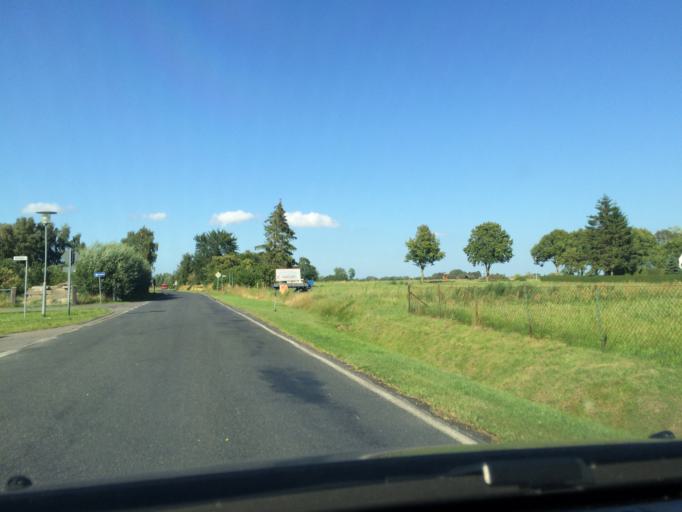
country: DE
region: Mecklenburg-Vorpommern
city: Niepars
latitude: 54.3450
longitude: 12.8949
